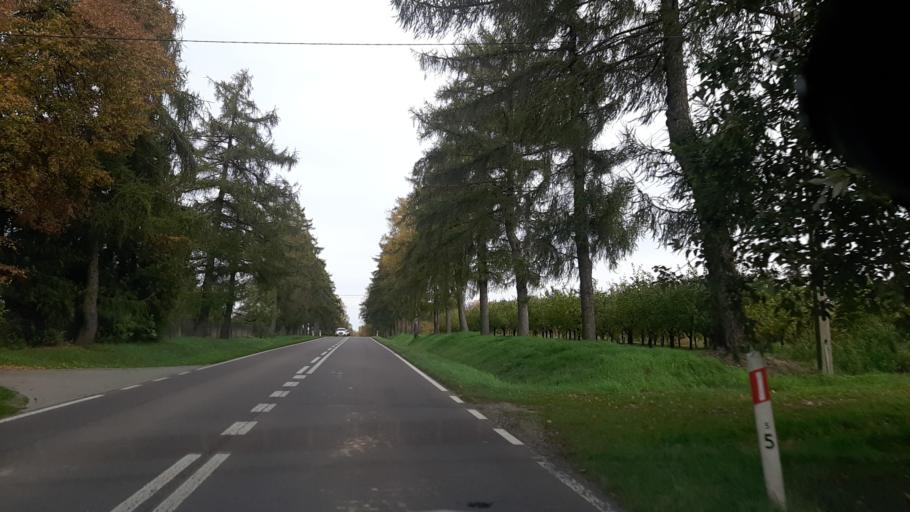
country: PL
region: Lublin Voivodeship
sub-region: Powiat pulawski
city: Naleczow
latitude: 51.3274
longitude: 22.2425
